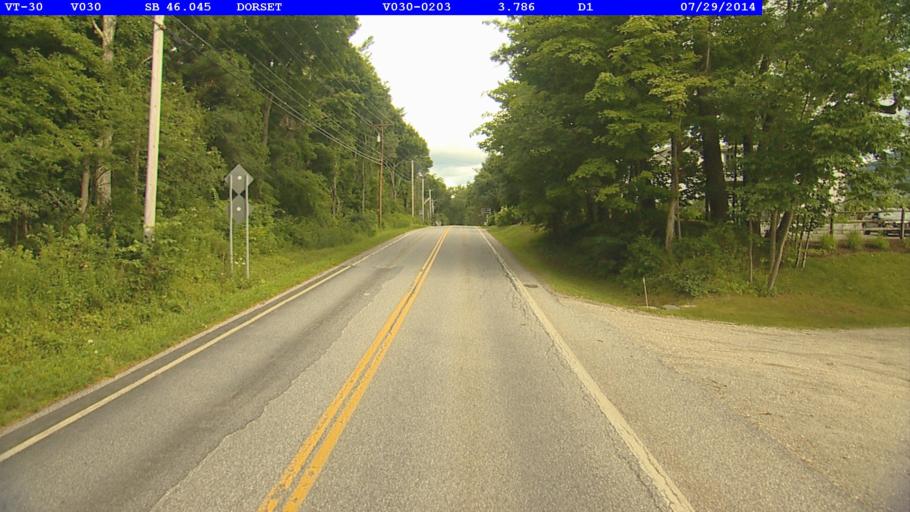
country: US
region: Vermont
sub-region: Bennington County
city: Manchester Center
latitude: 43.2598
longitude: -73.1034
